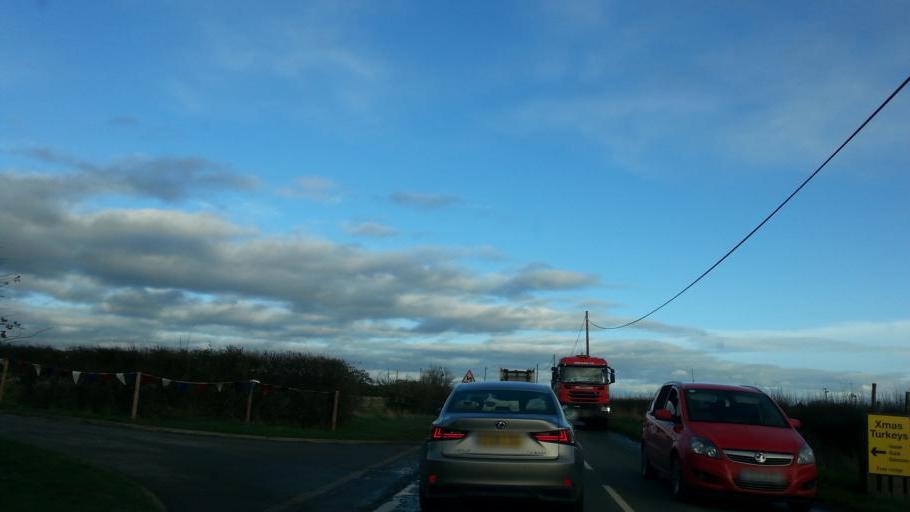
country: GB
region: England
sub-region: Oxfordshire
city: Faringdon
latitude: 51.6186
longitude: -1.5941
